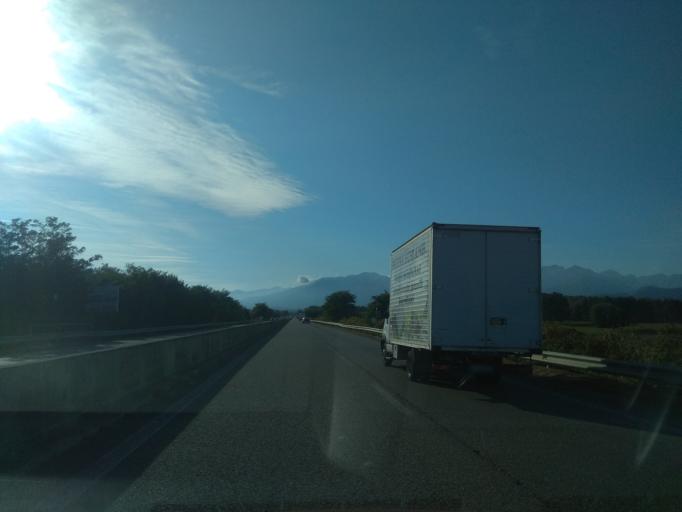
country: IT
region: Piedmont
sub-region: Provincia di Biella
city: Cossato
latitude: 45.5525
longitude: 8.1864
